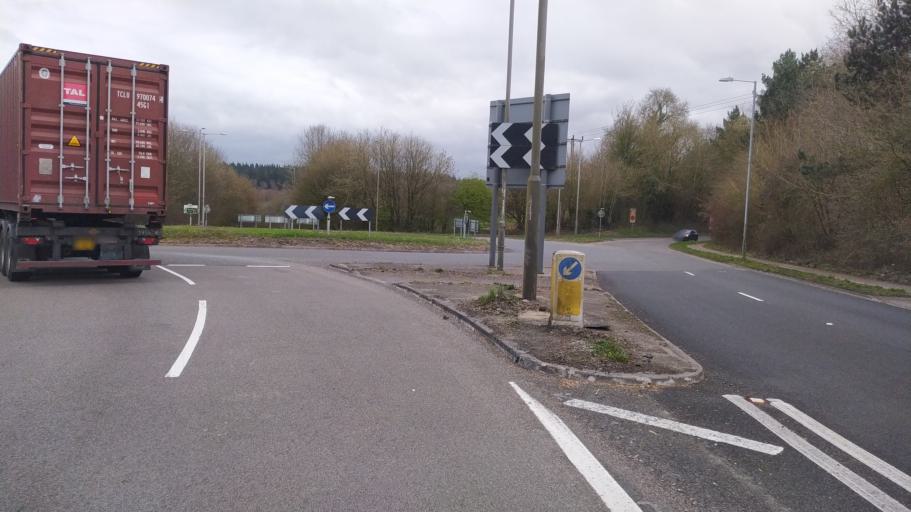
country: GB
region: England
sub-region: Wiltshire
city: Warminster
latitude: 51.1911
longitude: -2.1915
